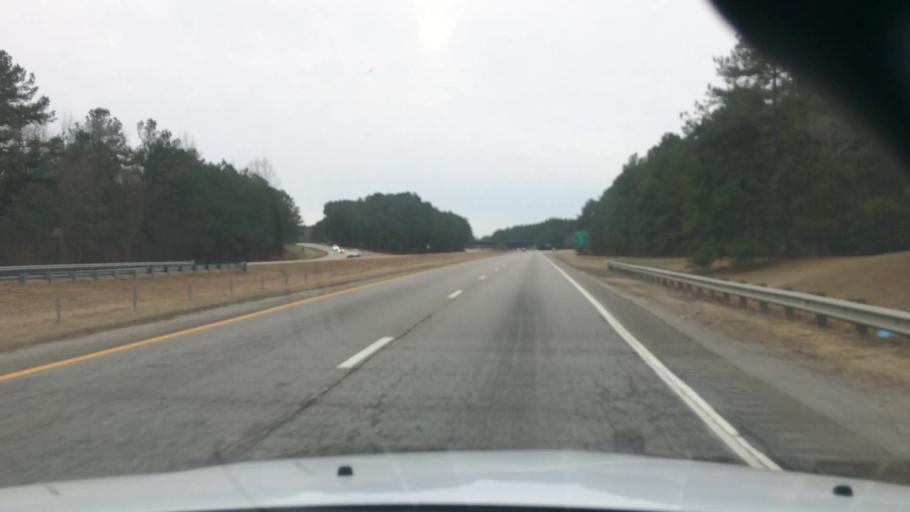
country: US
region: North Carolina
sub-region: Nash County
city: Nashville
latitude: 35.9739
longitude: -77.9856
